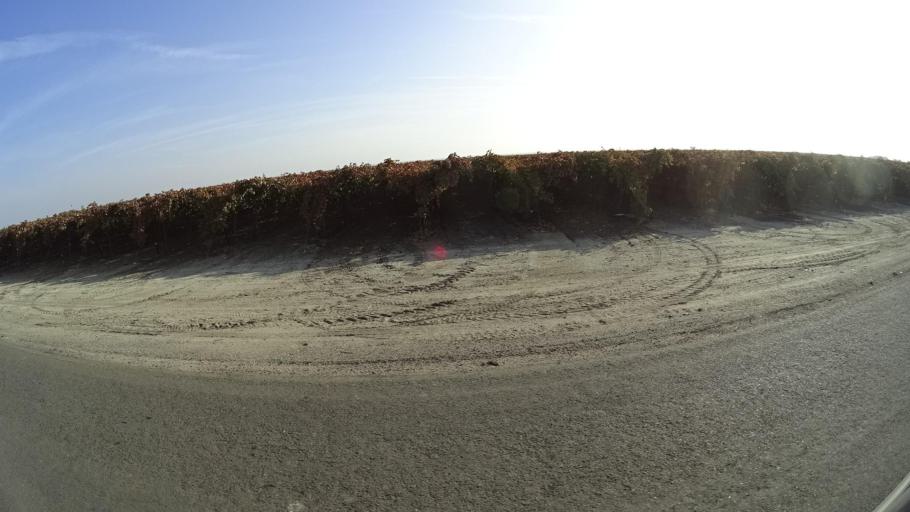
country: US
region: California
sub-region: Kern County
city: McFarland
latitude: 35.7097
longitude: -119.1872
